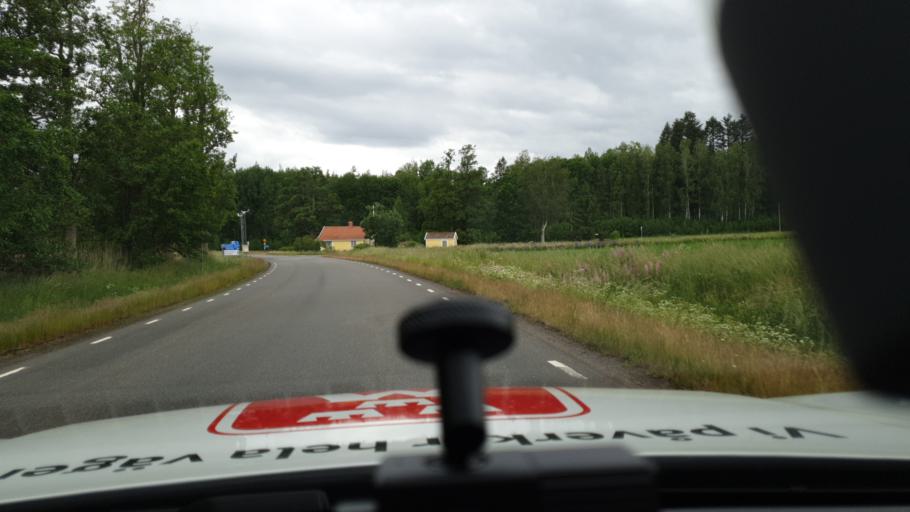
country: SE
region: Vaestra Goetaland
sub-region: Karlsborgs Kommun
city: Molltorp
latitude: 58.6822
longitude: 14.3396
